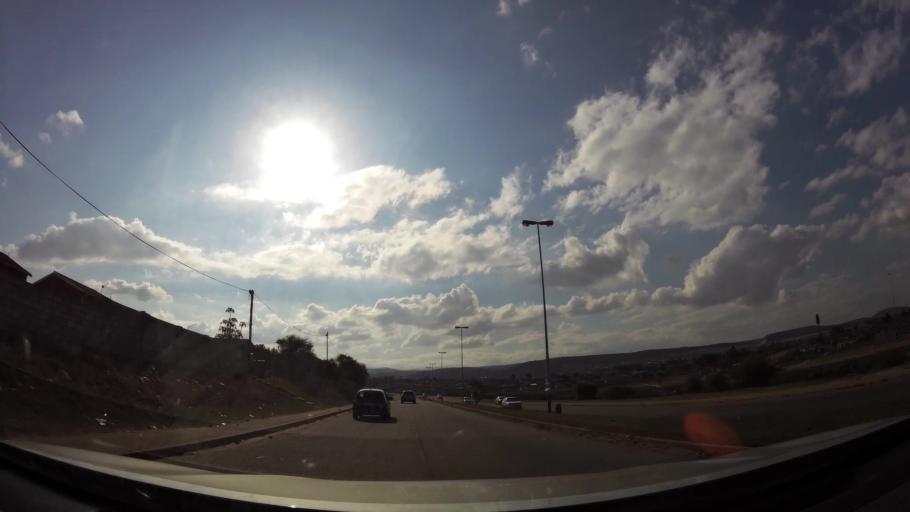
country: ZA
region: Eastern Cape
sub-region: Nelson Mandela Bay Metropolitan Municipality
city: Uitenhage
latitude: -33.7489
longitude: 25.3831
